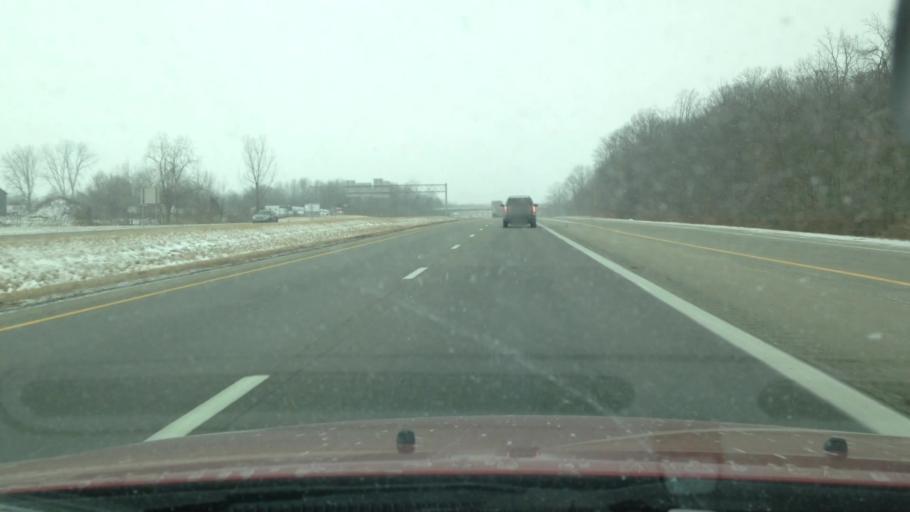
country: US
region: Ohio
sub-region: Montgomery County
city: Clayton
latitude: 39.8557
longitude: -84.3812
